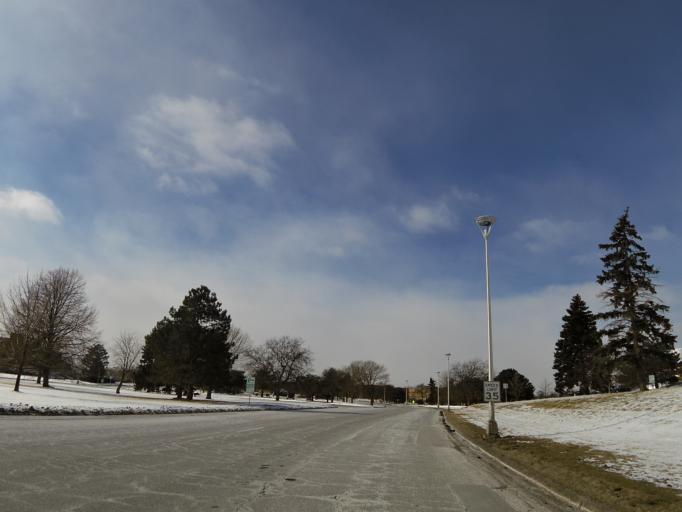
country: US
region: Minnesota
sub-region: Ramsey County
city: Maplewood
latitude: 44.9537
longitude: -92.9980
